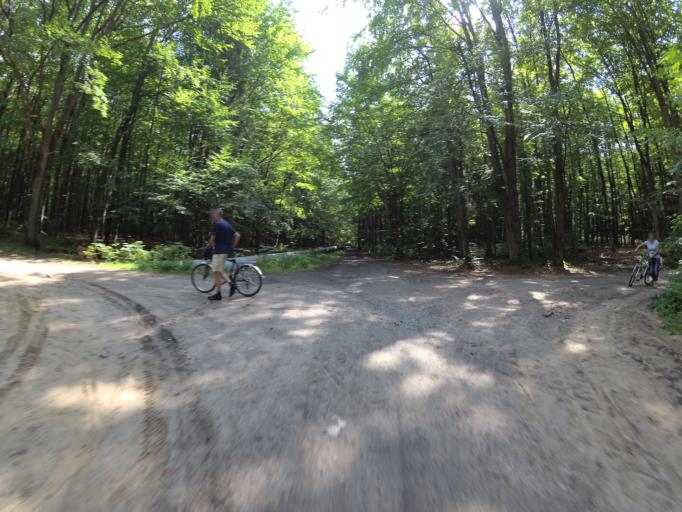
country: PL
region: Pomeranian Voivodeship
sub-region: Gdynia
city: Wielki Kack
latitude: 54.5086
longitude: 18.4886
